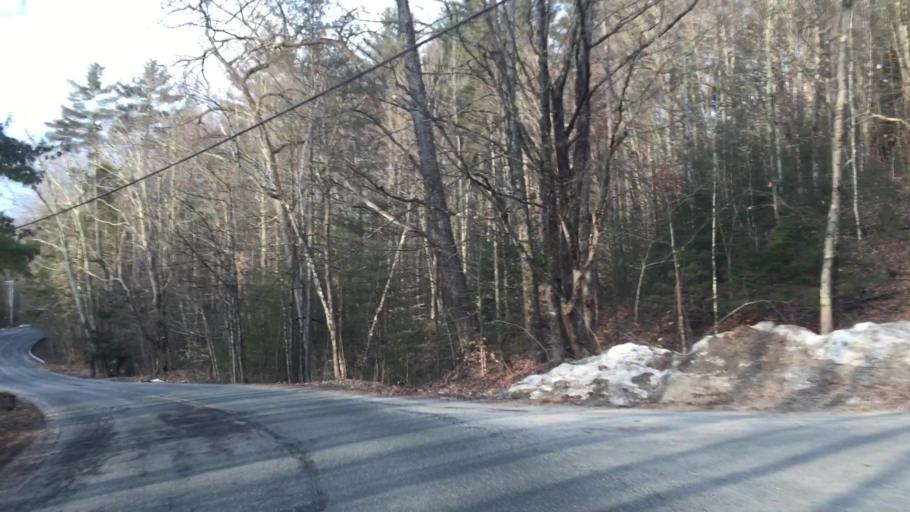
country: US
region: Massachusetts
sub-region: Berkshire County
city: New Marlborough
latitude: 42.1585
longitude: -73.2639
